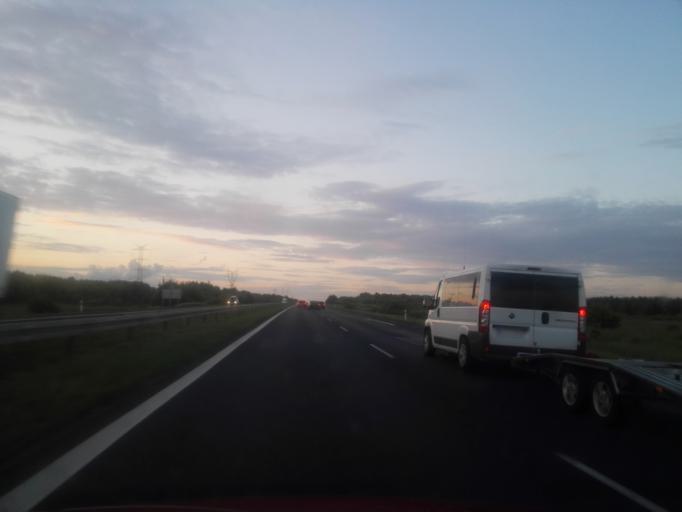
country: PL
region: Lodz Voivodeship
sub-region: Powiat radomszczanski
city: Radomsko
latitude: 51.0846
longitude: 19.3739
